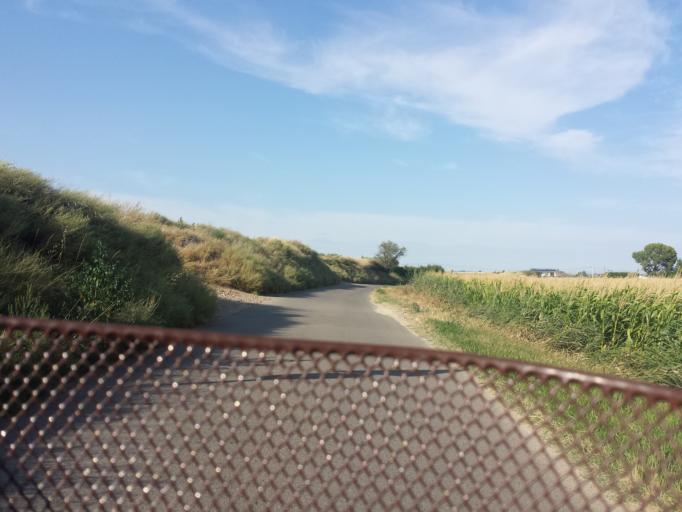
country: ES
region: Aragon
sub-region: Provincia de Zaragoza
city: Zaragoza
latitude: 41.7016
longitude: -0.8553
